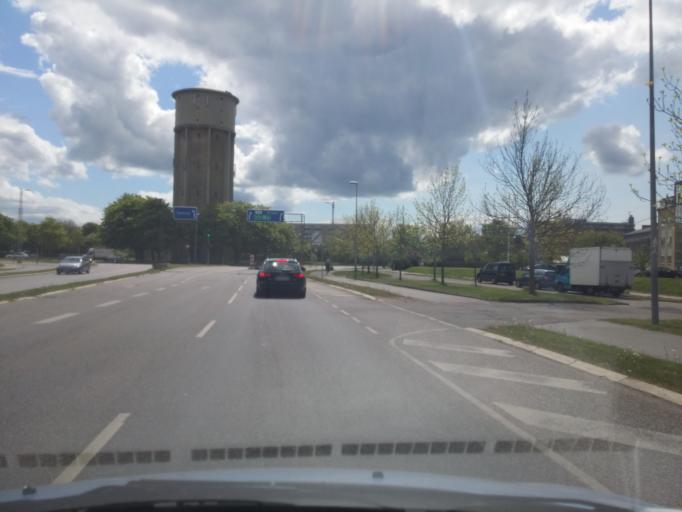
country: DK
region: Capital Region
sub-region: Tarnby Kommune
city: Tarnby
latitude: 55.6341
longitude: 12.6012
